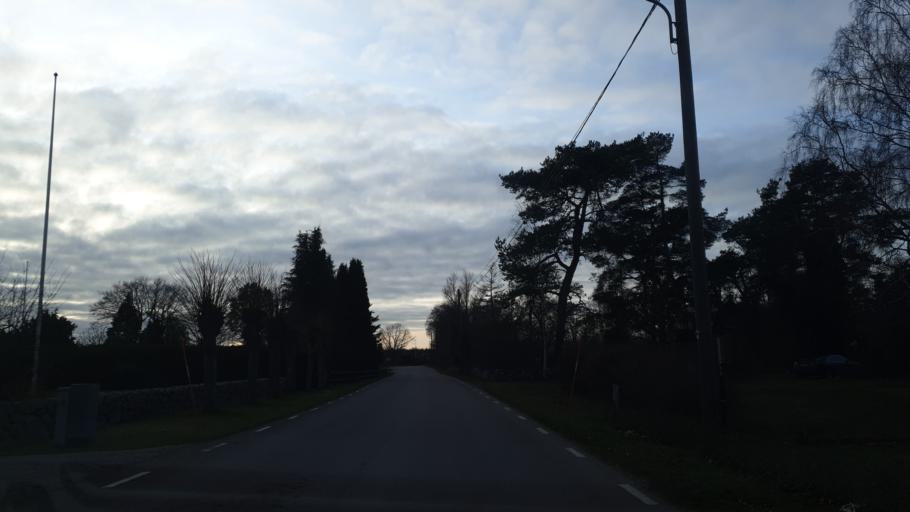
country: SE
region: Kalmar
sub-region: Torsas Kommun
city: Torsas
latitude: 56.2569
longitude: 16.0372
